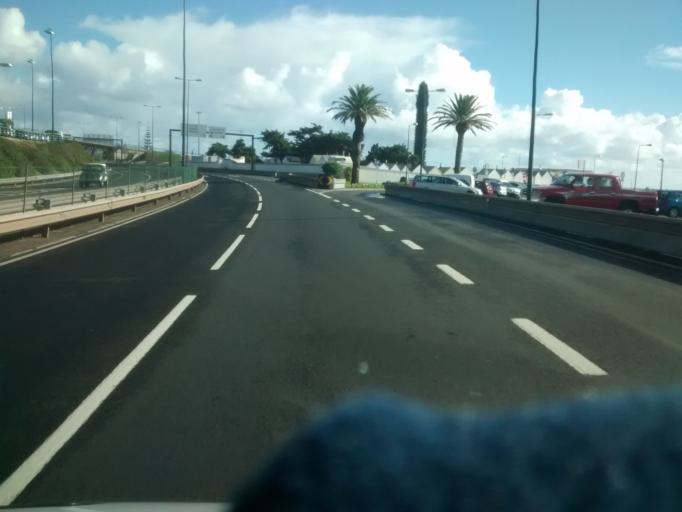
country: PT
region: Madeira
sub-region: Machico
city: Machico
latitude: 32.6911
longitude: -16.7755
